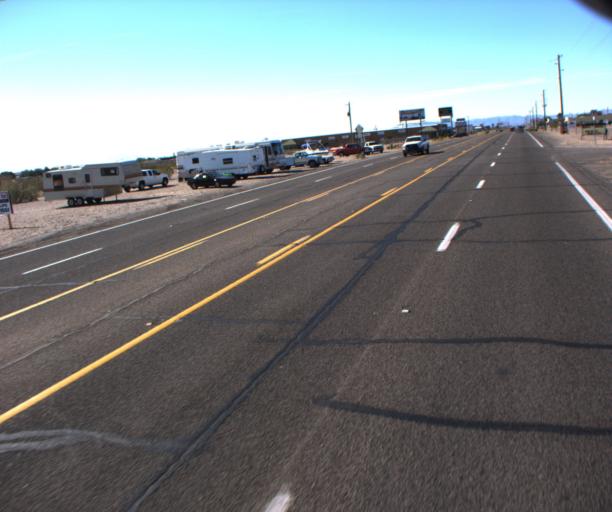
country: US
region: Arizona
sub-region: Mohave County
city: Mohave Valley
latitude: 34.9961
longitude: -114.5981
